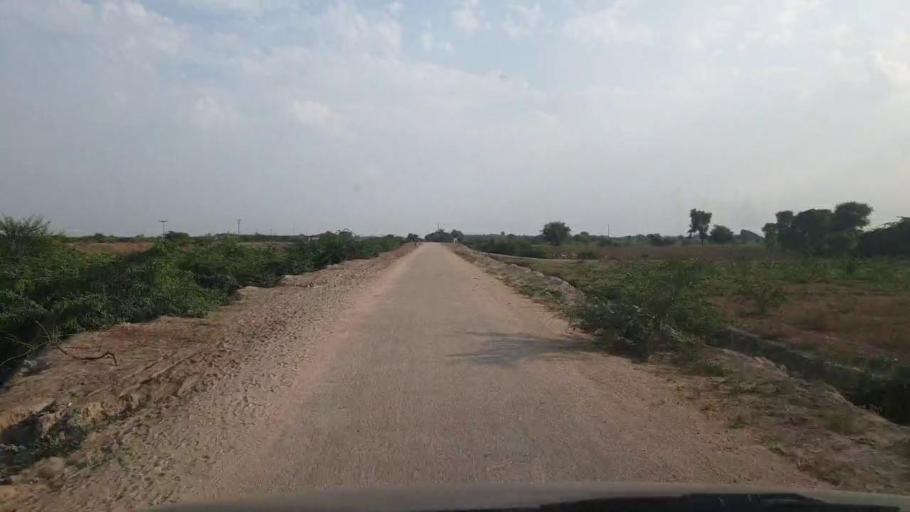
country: PK
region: Sindh
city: Badin
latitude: 24.5317
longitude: 68.6779
